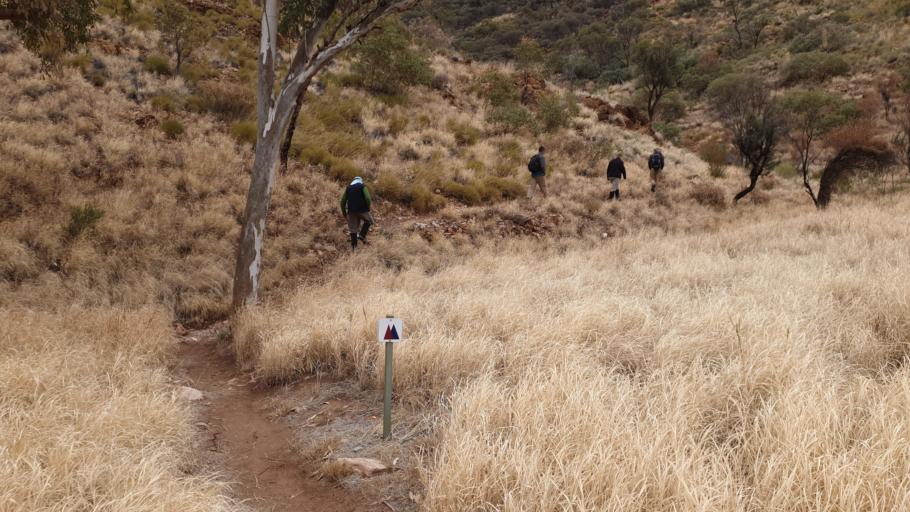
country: AU
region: Northern Territory
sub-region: Alice Springs
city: Alice Springs
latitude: -23.7792
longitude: 133.0711
